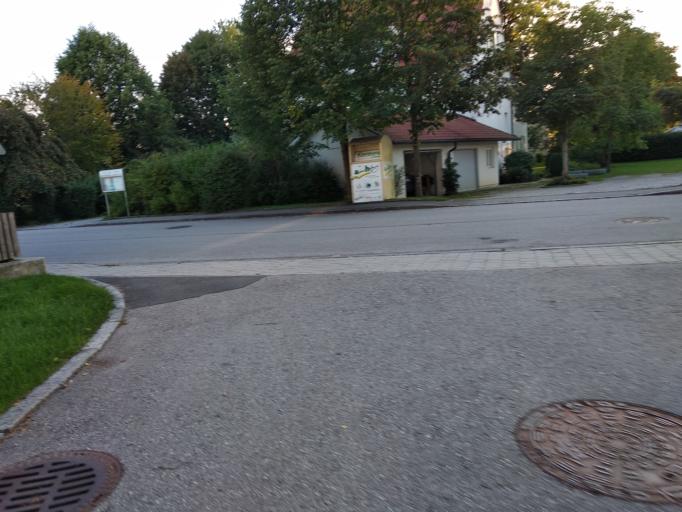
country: DE
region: Bavaria
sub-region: Upper Bavaria
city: Steinhoring
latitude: 48.0867
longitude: 12.0293
